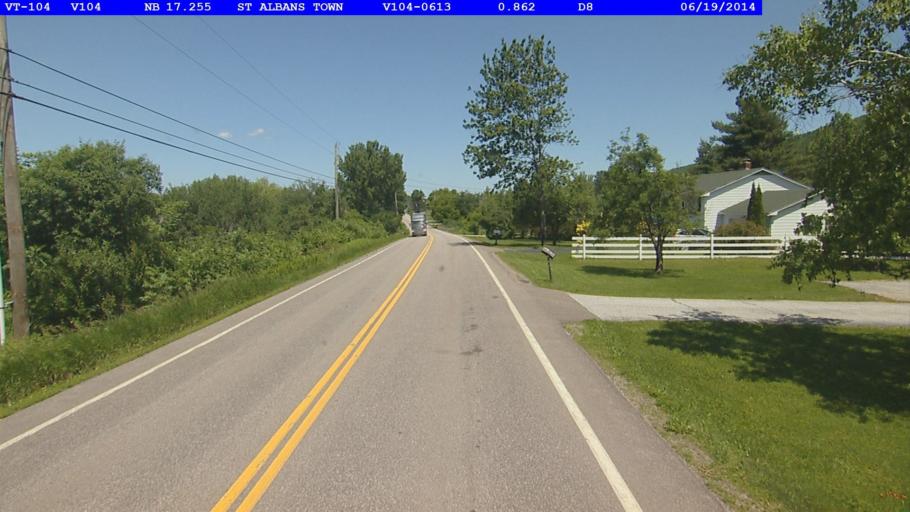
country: US
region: Vermont
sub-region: Franklin County
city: Saint Albans
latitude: 44.7858
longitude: -73.0761
